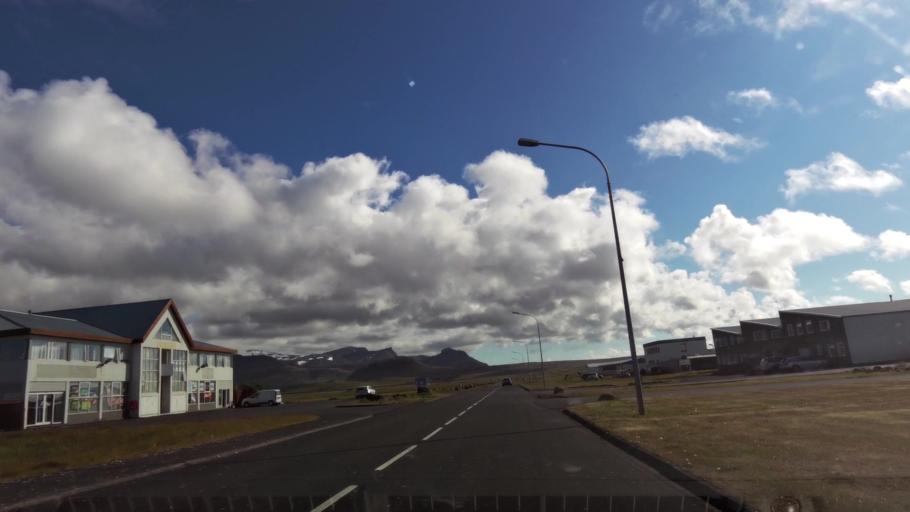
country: IS
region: West
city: Olafsvik
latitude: 64.9229
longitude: -23.8164
